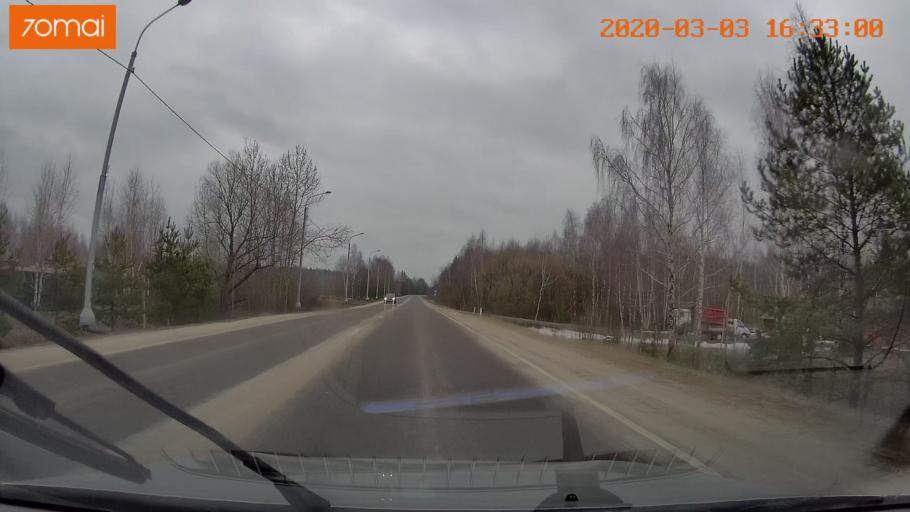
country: RU
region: Moskovskaya
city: Konobeyevo
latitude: 55.4181
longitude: 38.7371
